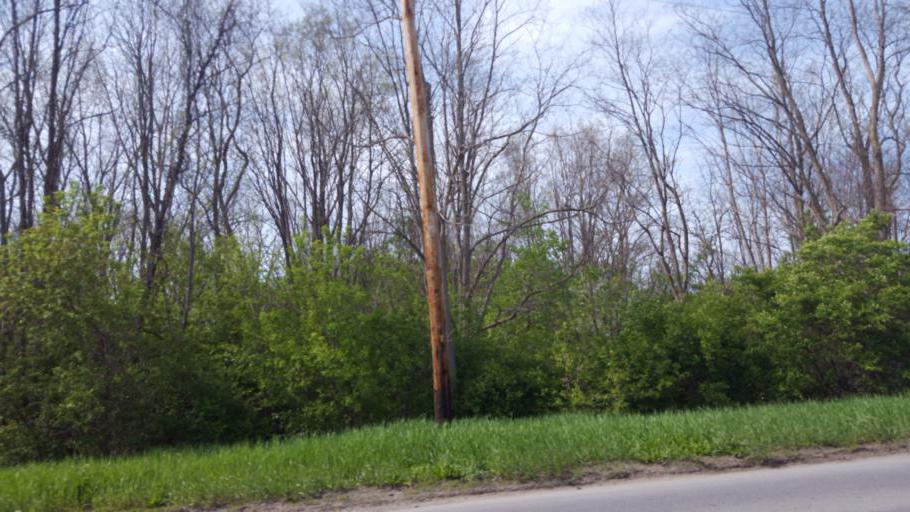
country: US
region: Ohio
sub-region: Lake County
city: Painesville
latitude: 41.7479
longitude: -81.2105
